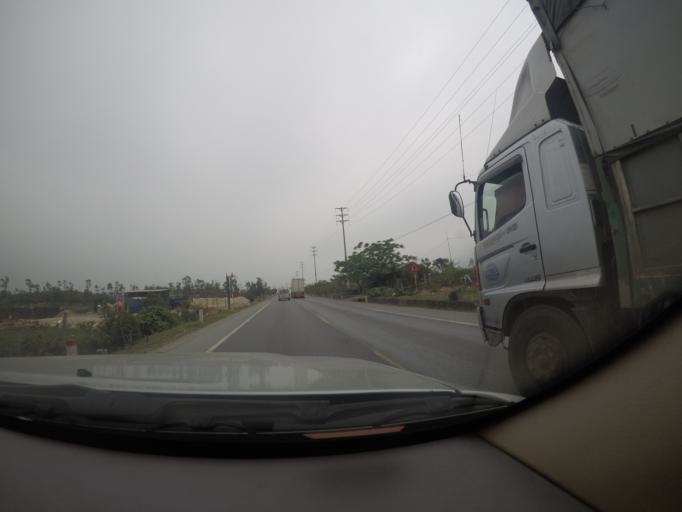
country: VN
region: Ha Tinh
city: Ky Anh
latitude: 18.0170
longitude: 106.3909
